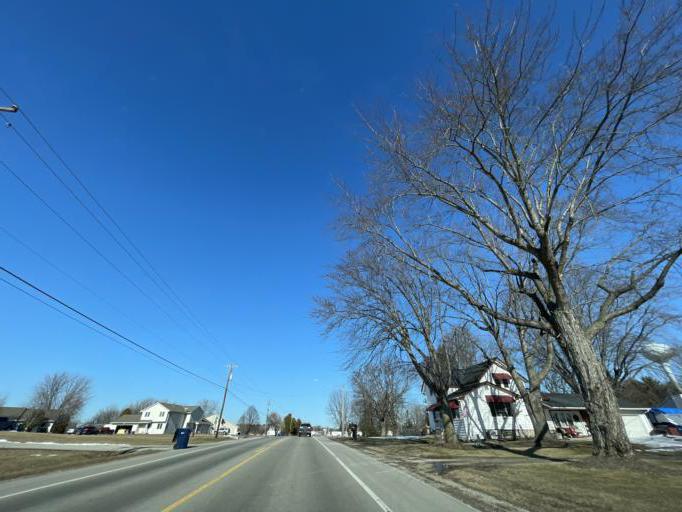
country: US
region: Wisconsin
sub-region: Brown County
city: Suamico
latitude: 44.6258
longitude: -88.0602
